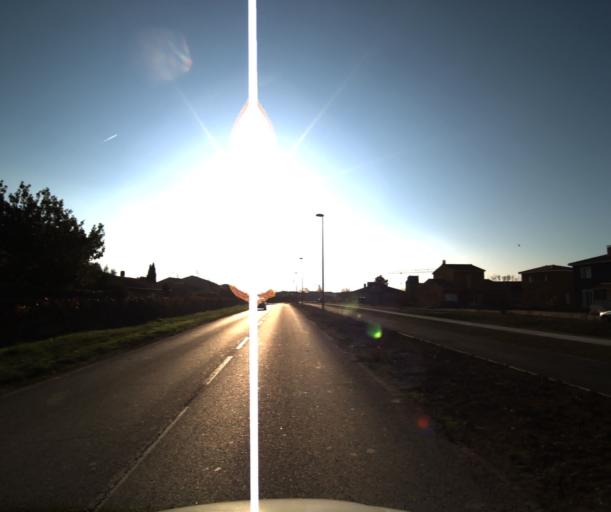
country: FR
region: Midi-Pyrenees
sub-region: Departement de la Haute-Garonne
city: Colomiers
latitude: 43.6238
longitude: 1.3300
